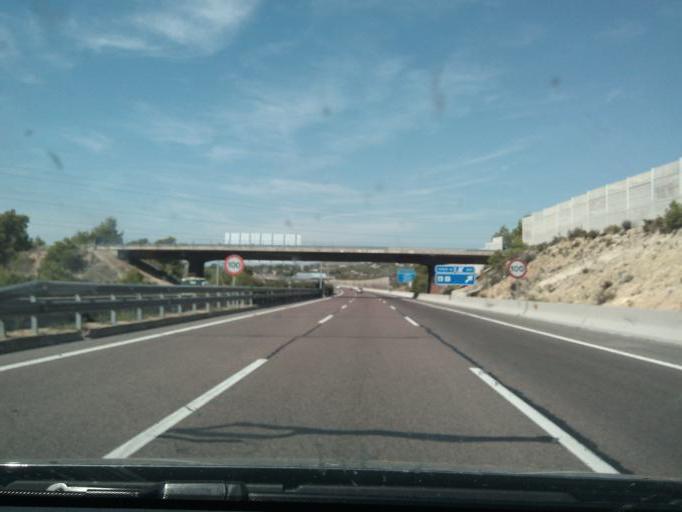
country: ES
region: Valencia
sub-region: Provincia de Valencia
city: Manises
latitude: 39.5138
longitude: -0.4917
